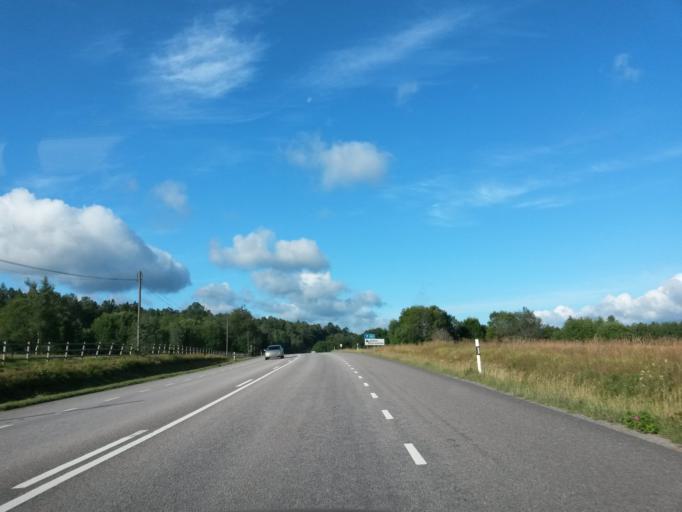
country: SE
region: Vaestra Goetaland
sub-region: Alingsas Kommun
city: Alingsas
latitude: 57.9373
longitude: 12.5813
